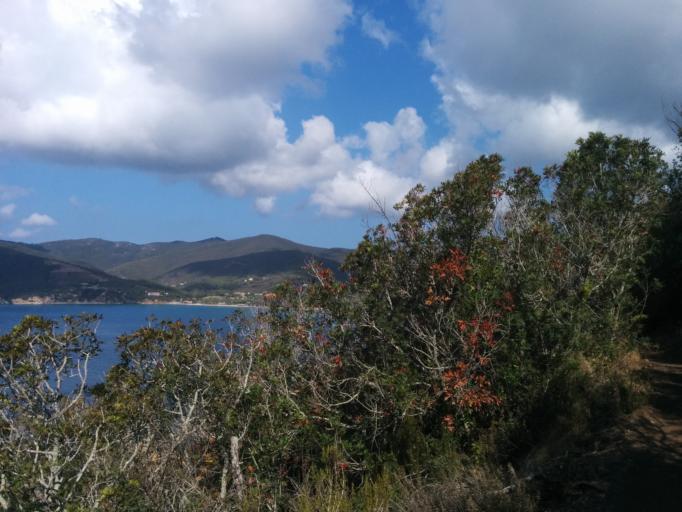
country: IT
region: Tuscany
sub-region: Provincia di Livorno
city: Portoferraio
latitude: 42.7501
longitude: 10.3150
